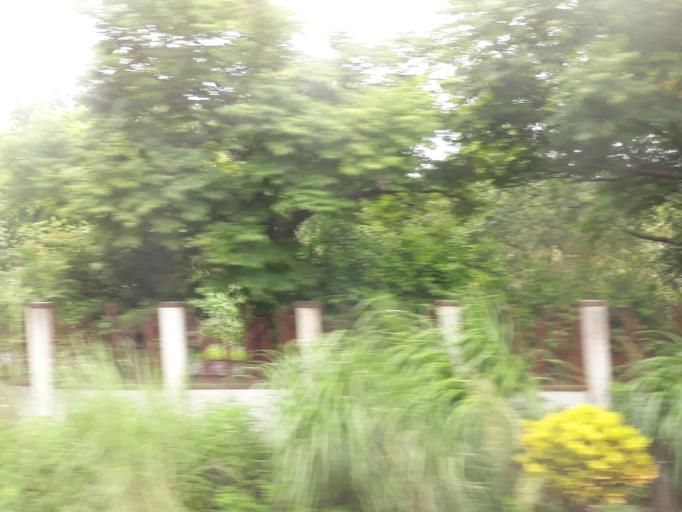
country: TW
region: Taiwan
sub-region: Yilan
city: Yilan
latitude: 24.6812
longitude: 121.7746
